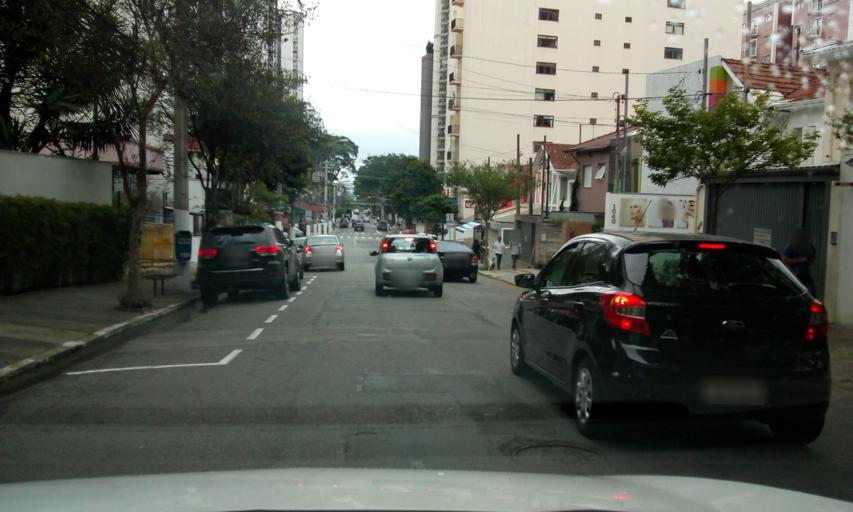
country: BR
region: Sao Paulo
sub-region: Sao Paulo
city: Sao Paulo
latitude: -23.5866
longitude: -46.6422
